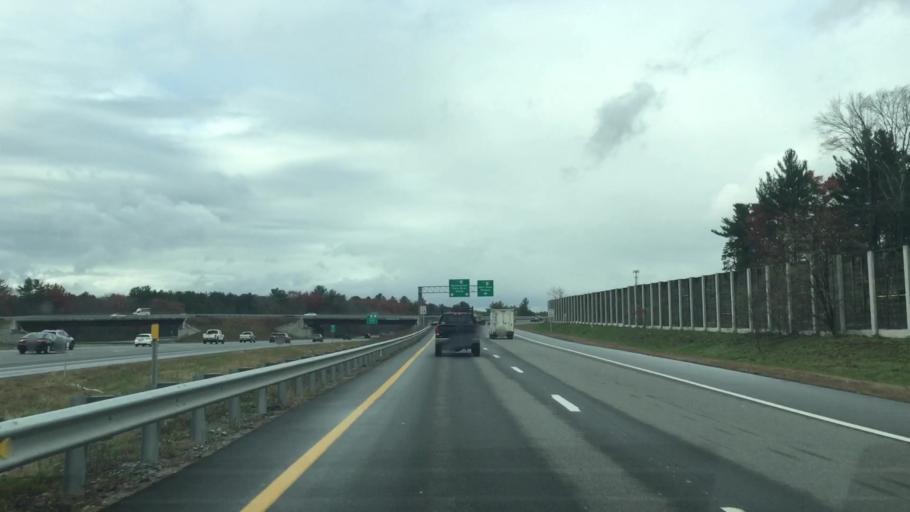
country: US
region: New Hampshire
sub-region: Rockingham County
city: Salem
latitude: 42.7592
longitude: -71.2305
